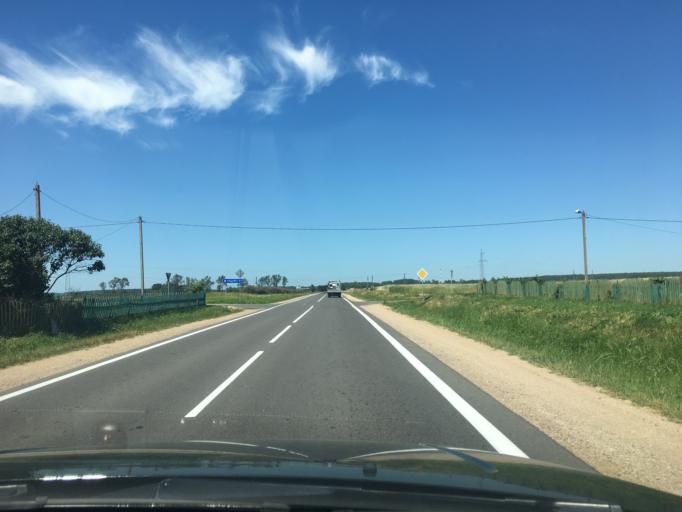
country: BY
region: Grodnenskaya
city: Hal'shany
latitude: 54.1008
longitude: 25.9143
